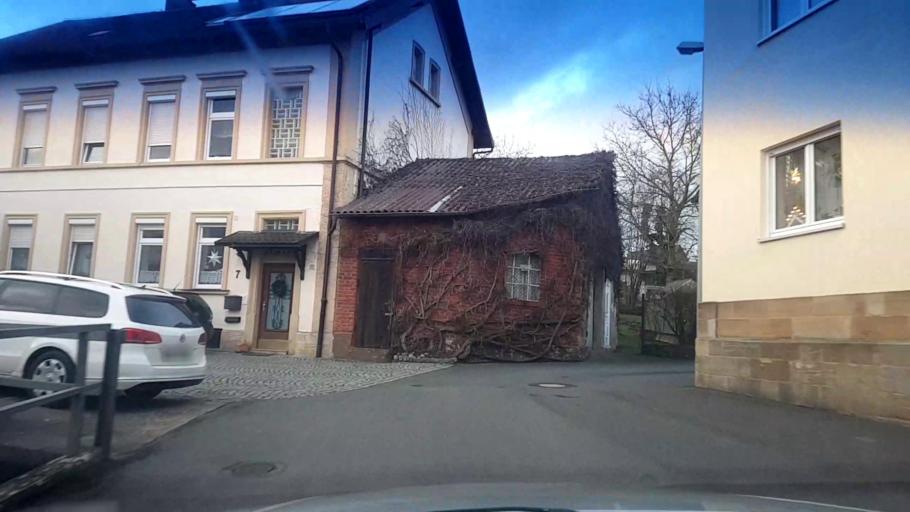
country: DE
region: Bavaria
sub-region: Upper Franconia
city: Strullendorf
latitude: 49.8591
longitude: 11.0076
